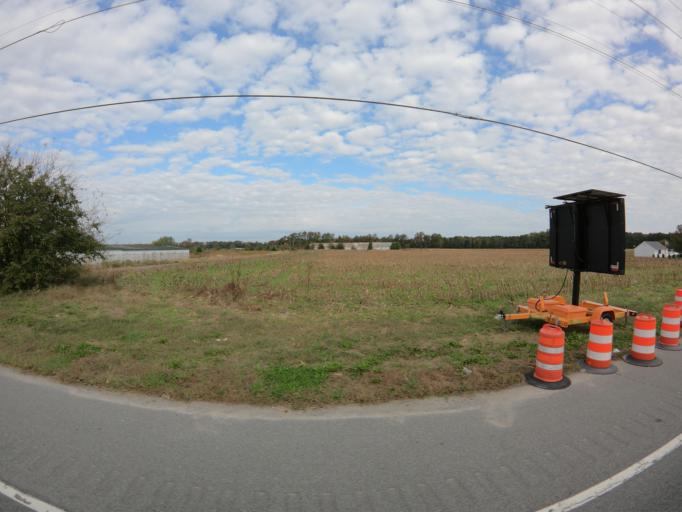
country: US
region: Delaware
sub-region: Sussex County
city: Georgetown
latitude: 38.7027
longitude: -75.3570
